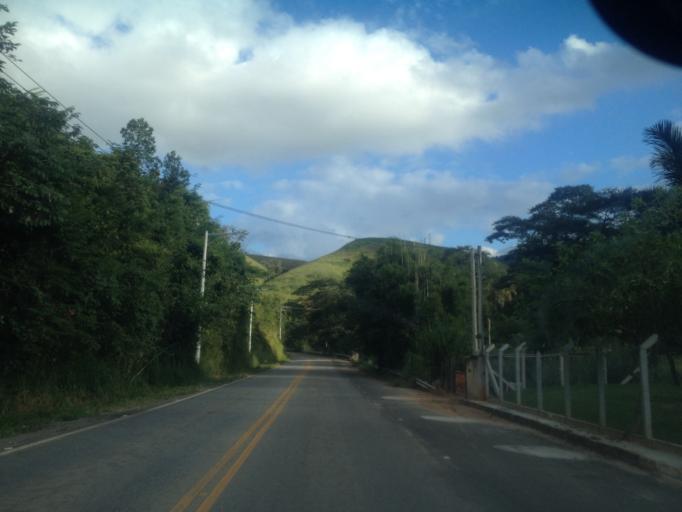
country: BR
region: Rio de Janeiro
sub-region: Quatis
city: Quatis
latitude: -22.2972
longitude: -44.2569
